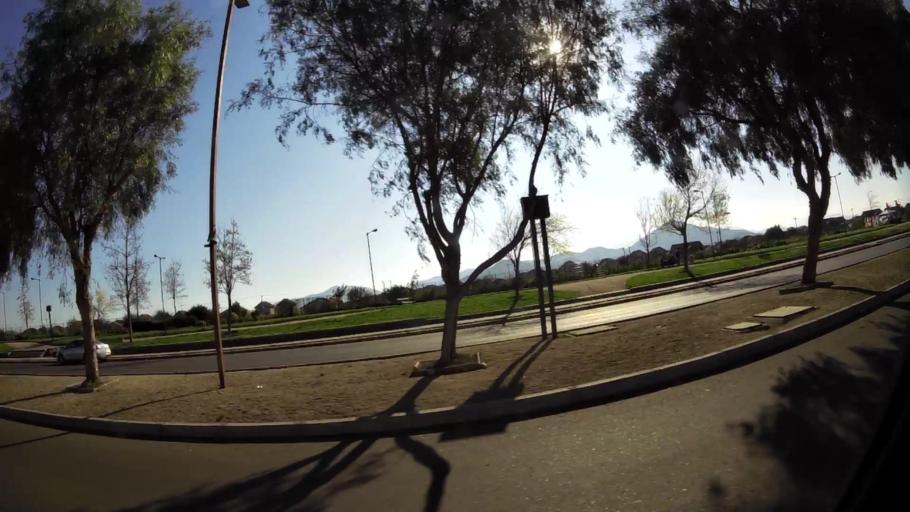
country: CL
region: Santiago Metropolitan
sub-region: Provincia de Santiago
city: Lo Prado
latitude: -33.4936
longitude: -70.7797
